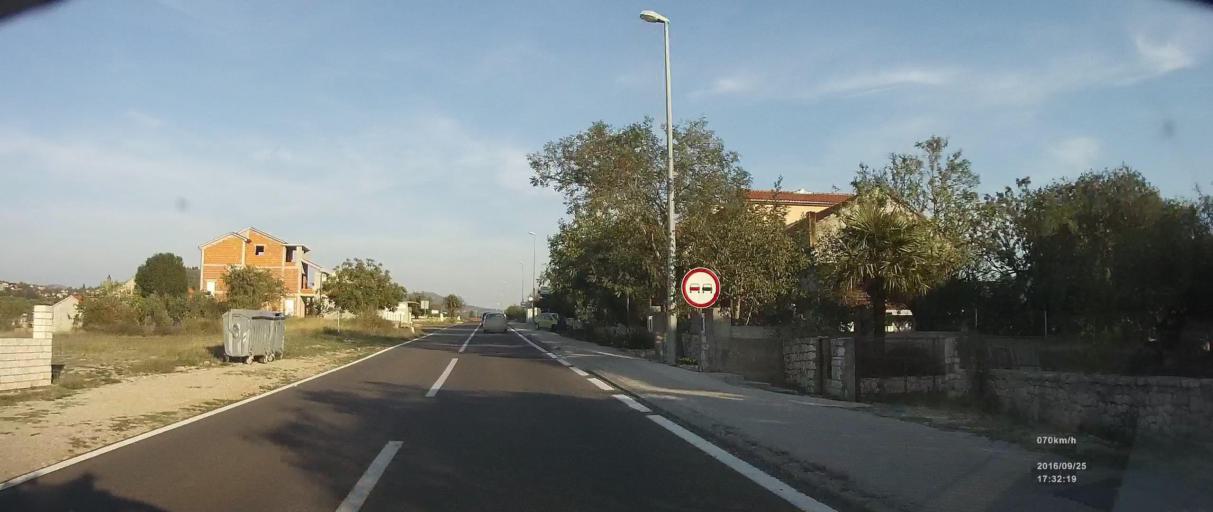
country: HR
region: Sibensko-Kniniska
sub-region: Grad Sibenik
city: Brodarica
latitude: 43.6751
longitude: 16.0009
